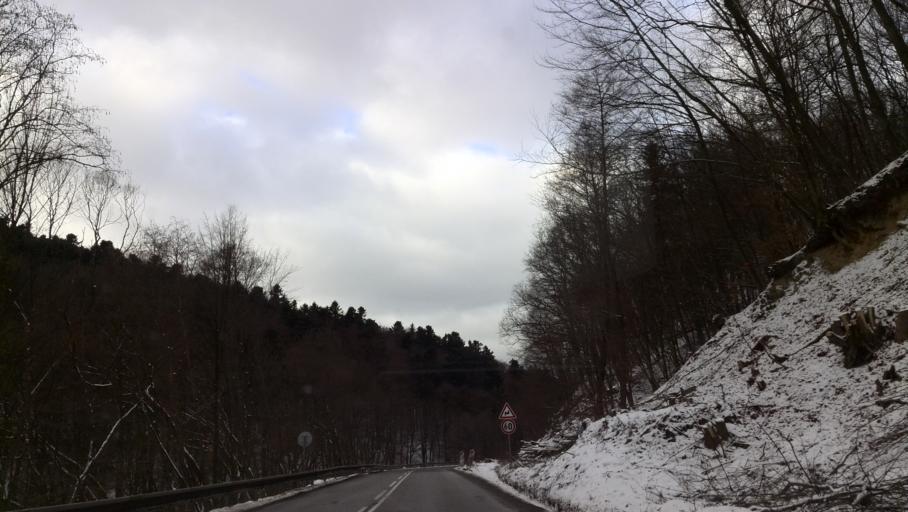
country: SK
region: Kosicky
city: Kosice
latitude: 48.7556
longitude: 21.1930
